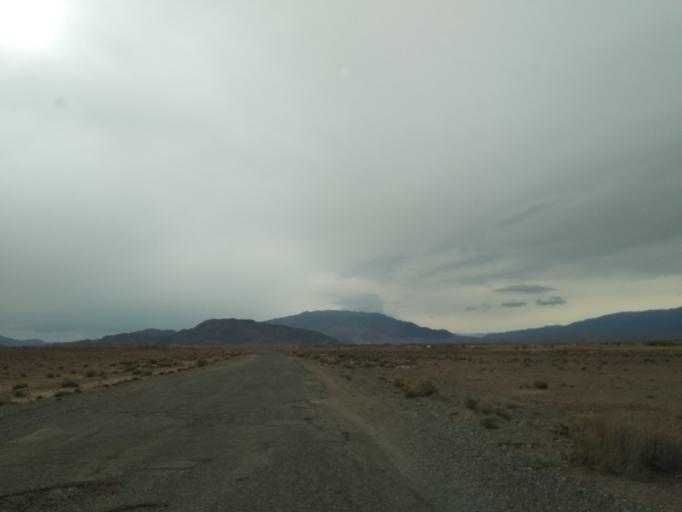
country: KG
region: Ysyk-Koel
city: Balykchy
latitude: 42.3199
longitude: 76.2263
